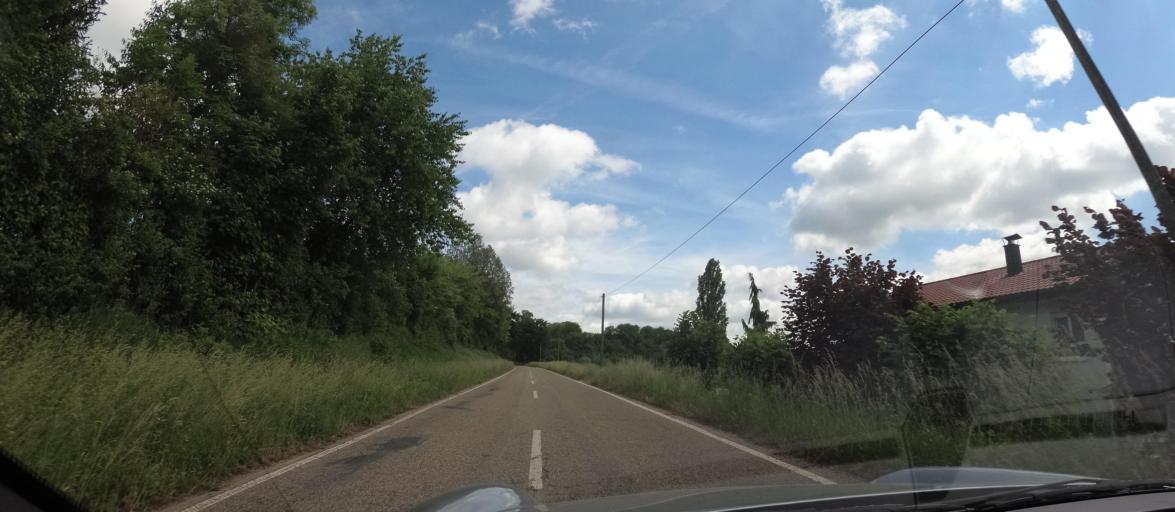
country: DE
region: Baden-Wuerttemberg
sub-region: Karlsruhe Region
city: Zaisenhausen
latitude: 49.1518
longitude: 8.8108
